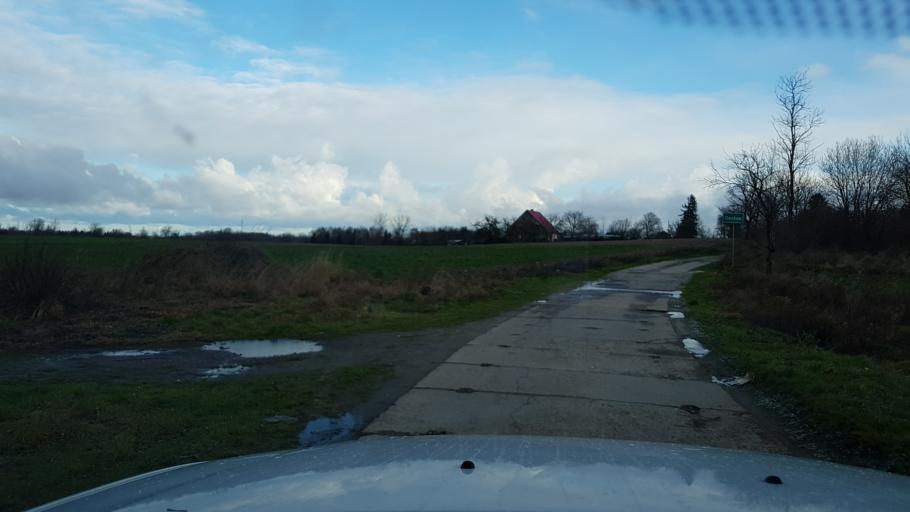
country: PL
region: West Pomeranian Voivodeship
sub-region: Powiat gryficki
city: Brojce
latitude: 54.0477
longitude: 15.3940
